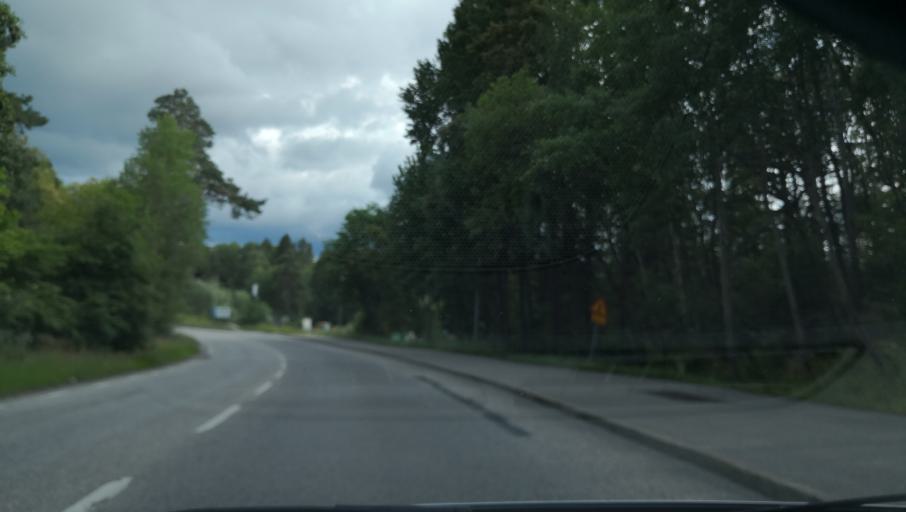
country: SE
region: Stockholm
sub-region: Stockholms Kommun
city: Arsta
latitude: 59.2579
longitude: 18.0453
